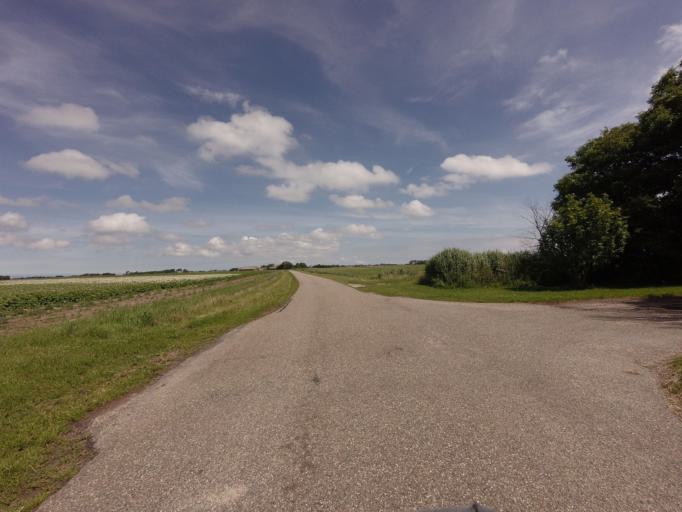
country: NL
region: North Holland
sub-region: Gemeente Texel
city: Den Burg
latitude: 53.0605
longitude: 4.8491
